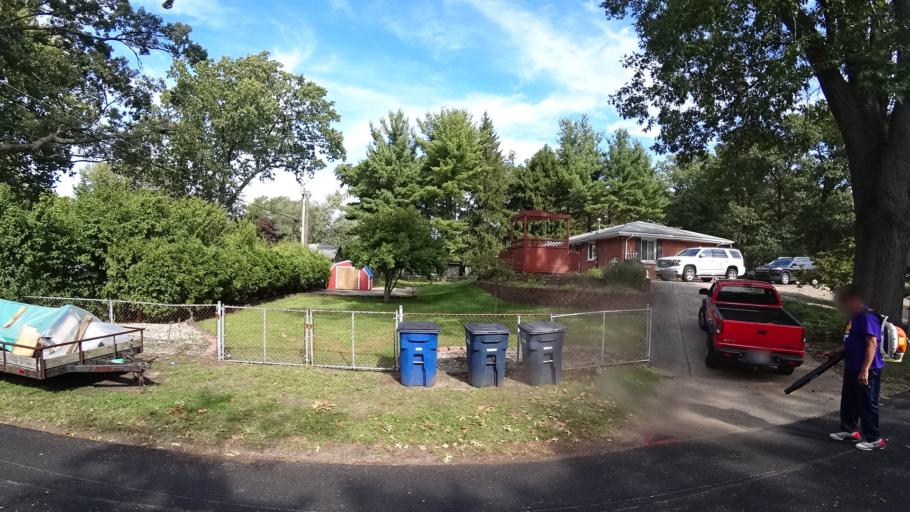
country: US
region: Indiana
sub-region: LaPorte County
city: Michigan City
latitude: 41.7189
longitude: -86.8739
